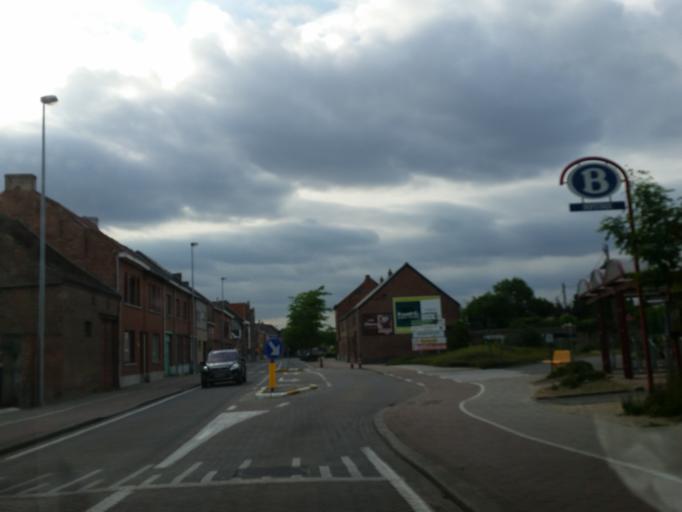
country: BE
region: Flanders
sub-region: Provincie Vlaams-Brabant
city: Zemst
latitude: 50.9879
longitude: 4.4967
